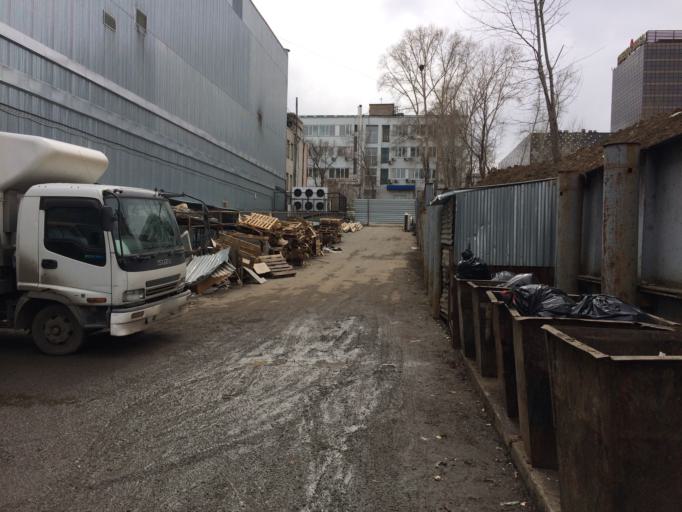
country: RU
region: Khabarovsk Krai
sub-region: Khabarovskiy Rayon
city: Khabarovsk
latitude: 48.4846
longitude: 135.0948
